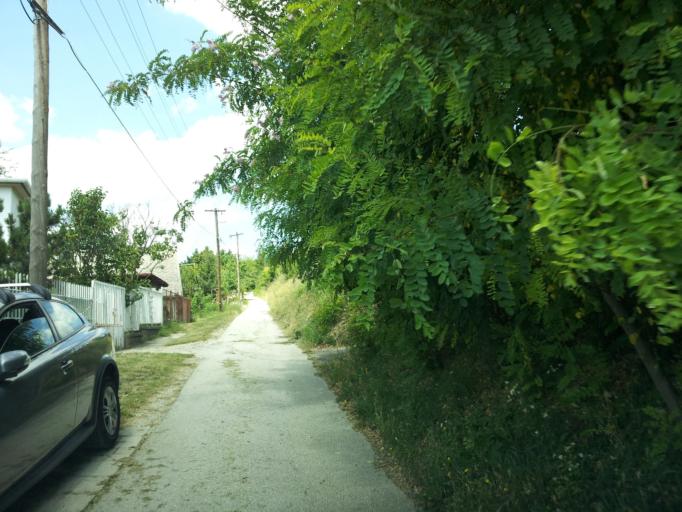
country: HU
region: Veszprem
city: Balatonkenese
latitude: 47.0373
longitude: 18.1166
